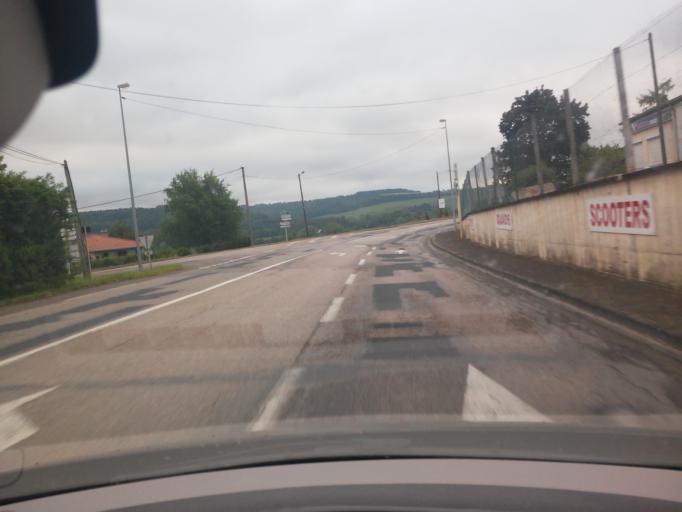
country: FR
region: Lorraine
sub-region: Departement de la Meuse
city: Saint-Mihiel
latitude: 48.9026
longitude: 5.5194
